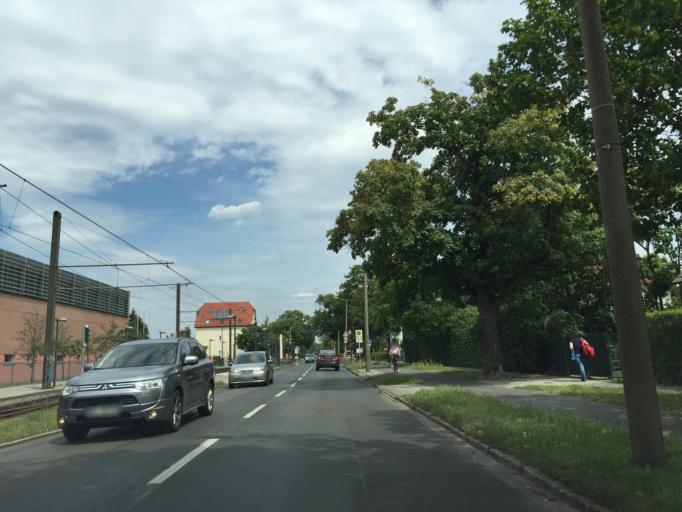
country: DE
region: Berlin
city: Mahlsdorf
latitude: 52.4930
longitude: 13.6092
